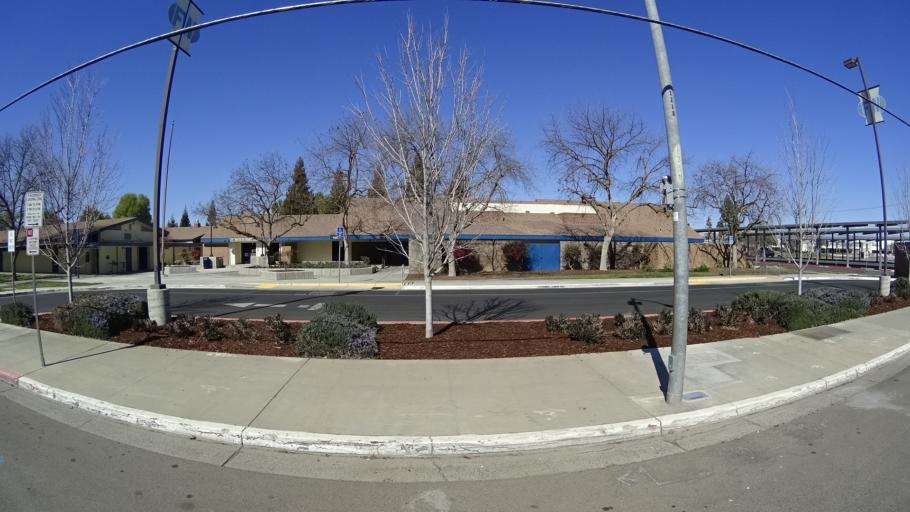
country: US
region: California
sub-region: Fresno County
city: Clovis
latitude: 36.8592
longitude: -119.7670
